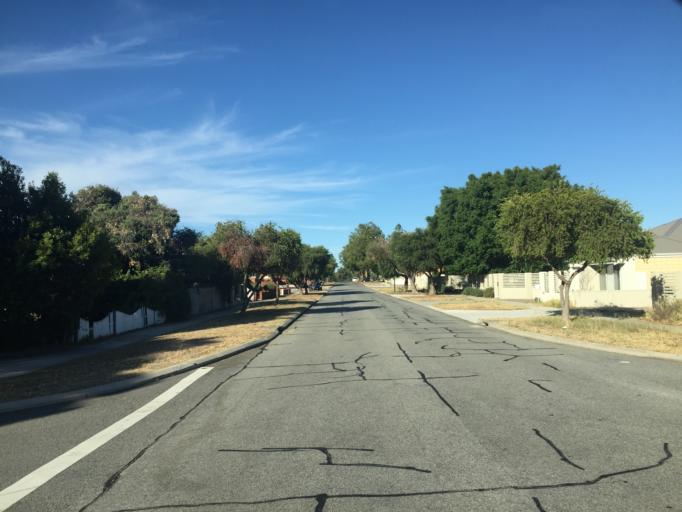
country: AU
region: Western Australia
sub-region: Belmont
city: Rivervale
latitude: -31.9630
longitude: 115.9169
